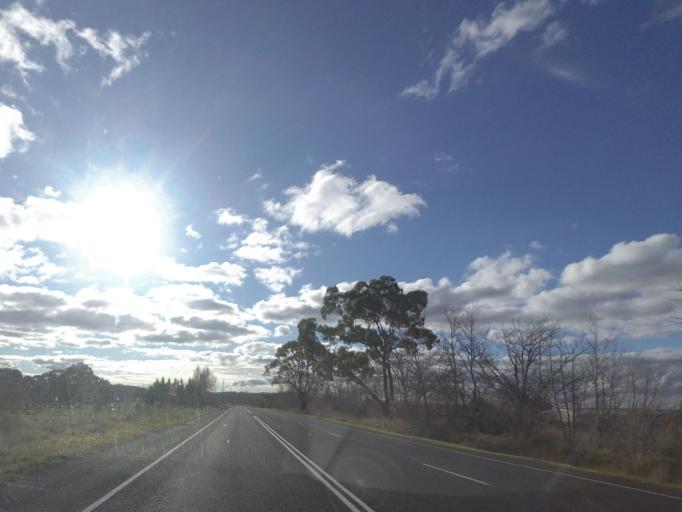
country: AU
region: Victoria
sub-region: Mount Alexander
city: Castlemaine
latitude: -37.1476
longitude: 144.3507
